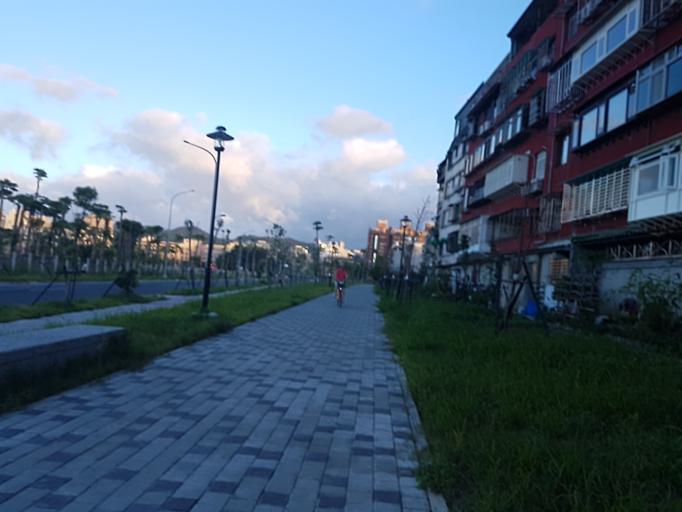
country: TW
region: Taipei
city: Taipei
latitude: 24.9770
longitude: 121.5279
